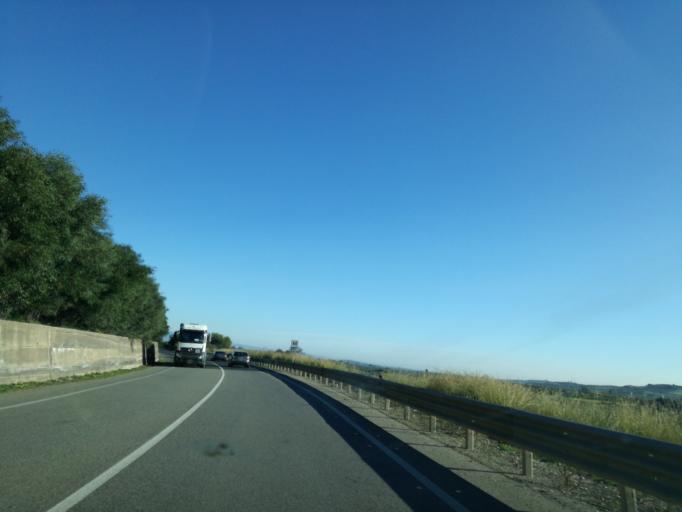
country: IT
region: Sicily
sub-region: Catania
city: Ramacca
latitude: 37.3651
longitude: 14.7187
